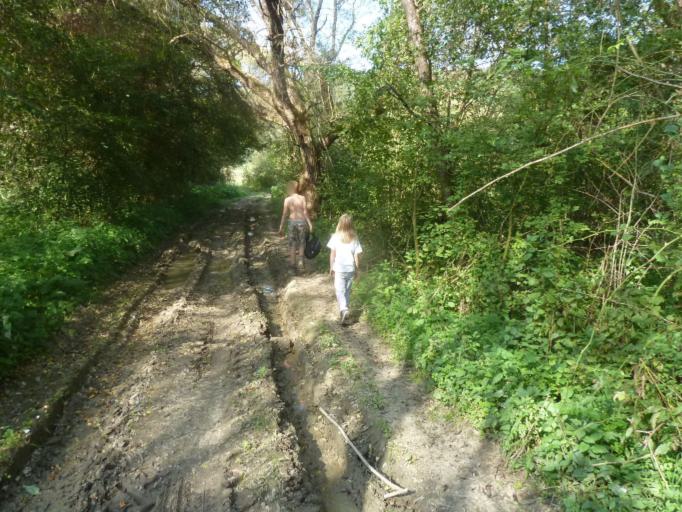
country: HU
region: Nograd
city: Romhany
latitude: 47.8689
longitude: 19.2638
